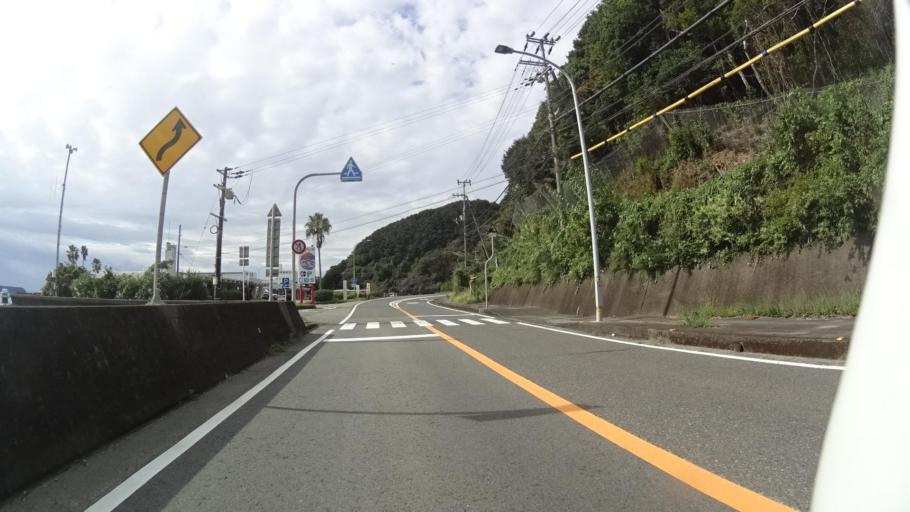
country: JP
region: Wakayama
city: Shingu
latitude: 33.4822
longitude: 135.7458
